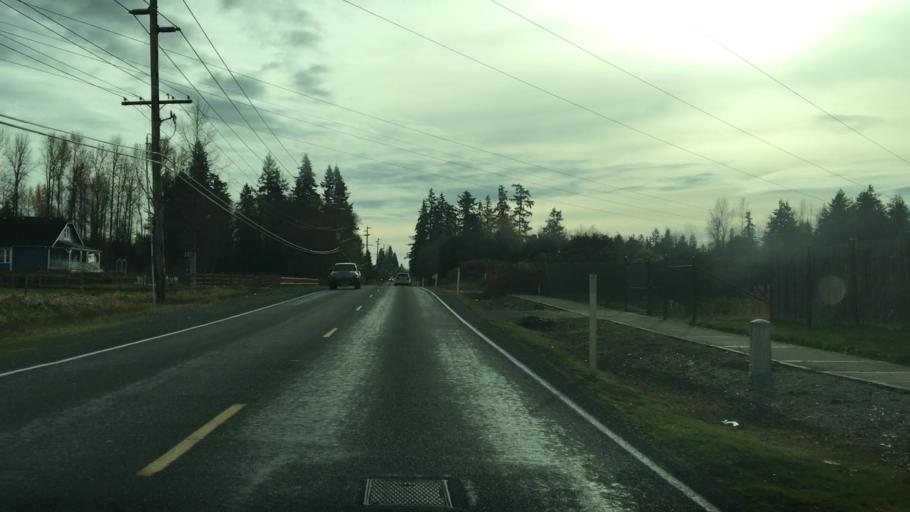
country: US
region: Washington
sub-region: Pierce County
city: South Hill
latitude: 47.1315
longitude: -122.3149
